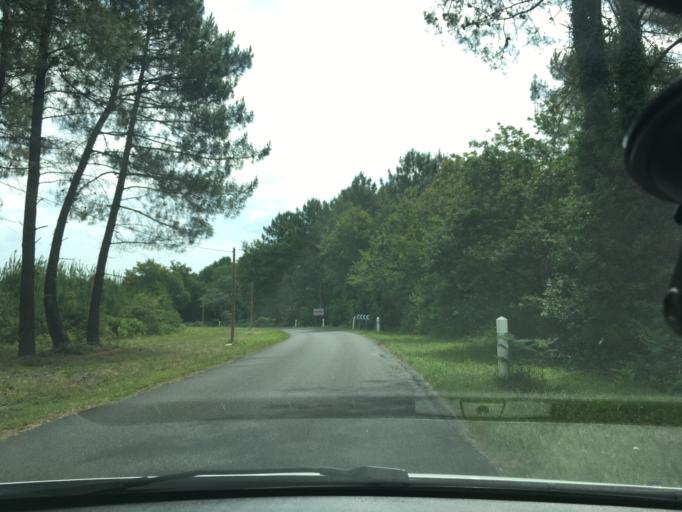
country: FR
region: Aquitaine
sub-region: Departement de la Gironde
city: Gaillan-en-Medoc
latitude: 45.3354
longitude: -1.0024
